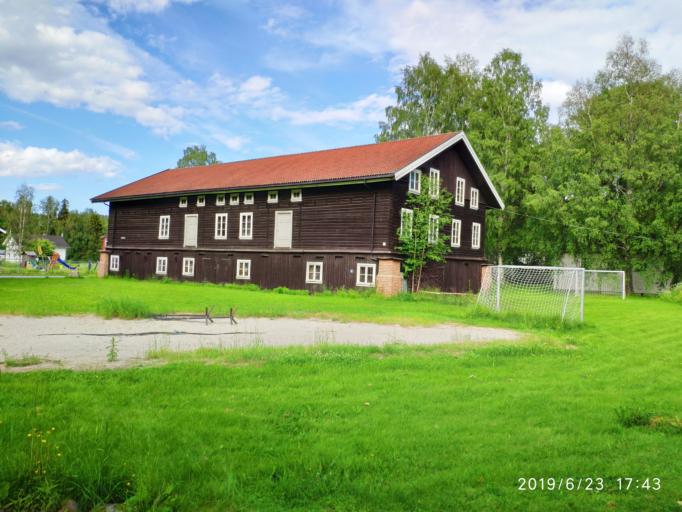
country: NO
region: Buskerud
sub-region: Ringerike
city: Honefoss
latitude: 60.1881
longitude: 10.3033
